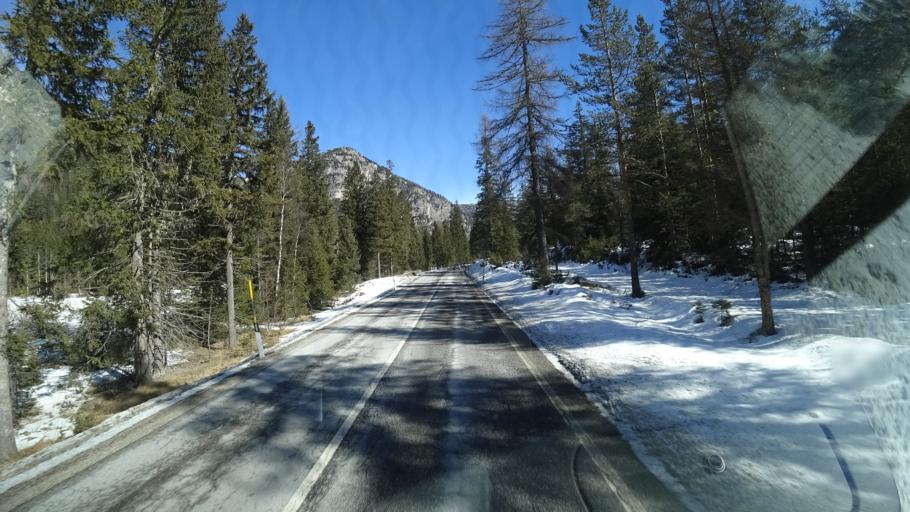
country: IT
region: Veneto
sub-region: Provincia di Belluno
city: Cortina d'Ampezzo
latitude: 46.6170
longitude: 12.1706
